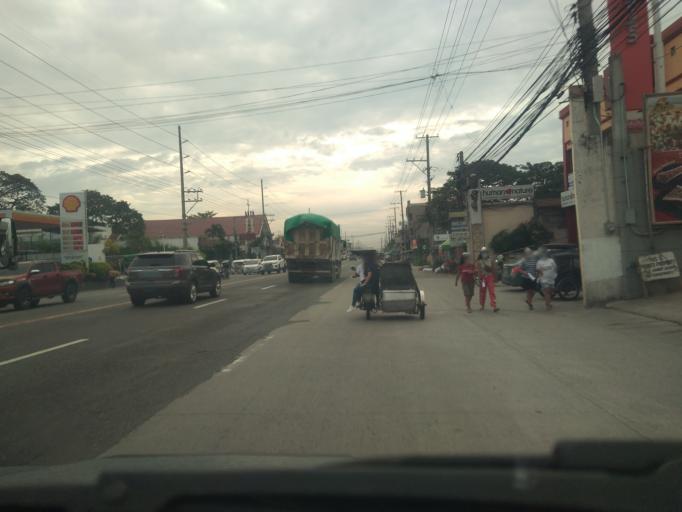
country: PH
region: Central Luzon
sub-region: Province of Pampanga
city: Magliman
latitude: 15.0481
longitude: 120.6676
